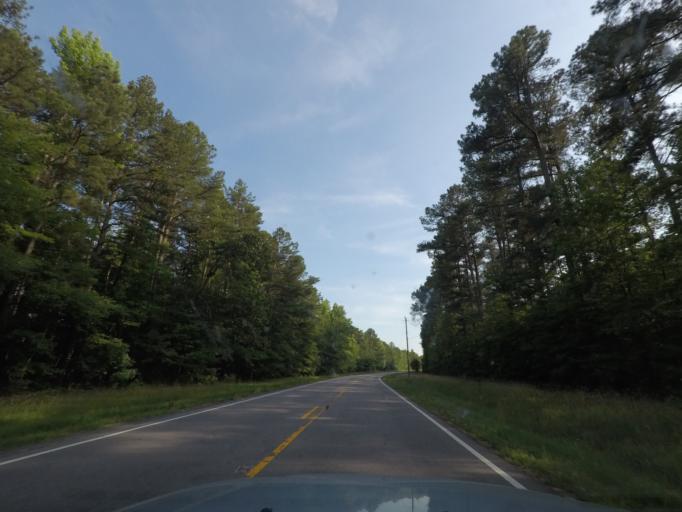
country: US
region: North Carolina
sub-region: Granville County
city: Oxford
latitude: 36.4240
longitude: -78.5841
